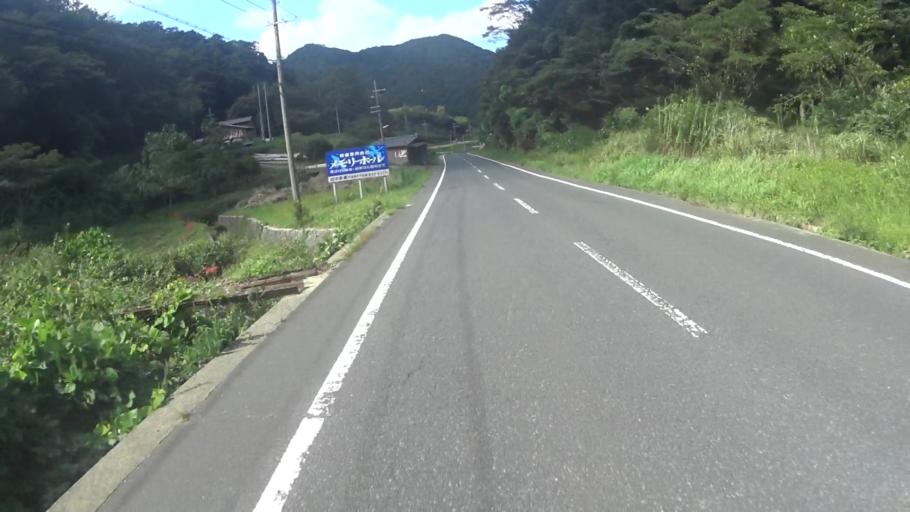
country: JP
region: Kyoto
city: Miyazu
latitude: 35.6905
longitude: 135.2781
